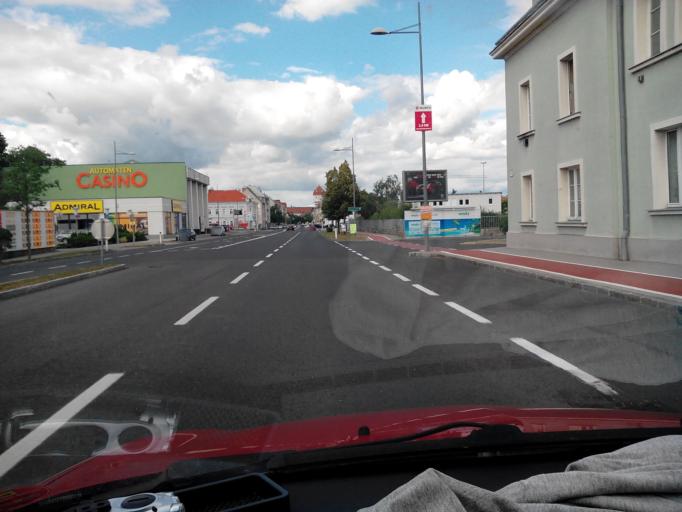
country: AT
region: Lower Austria
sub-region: Wiener Neustadt Stadt
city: Wiener Neustadt
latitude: 47.8033
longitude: 16.2345
